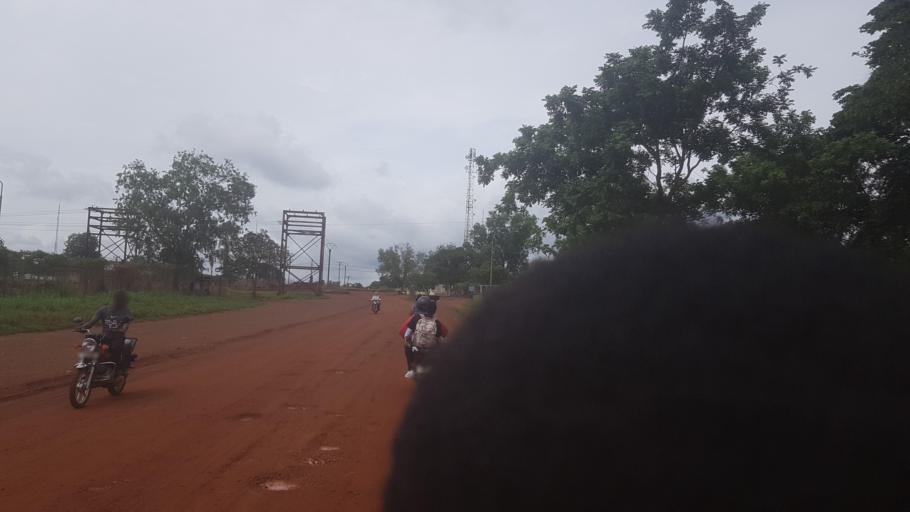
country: SL
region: Southern Province
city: Mogbwemo
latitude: 7.7678
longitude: -12.2960
